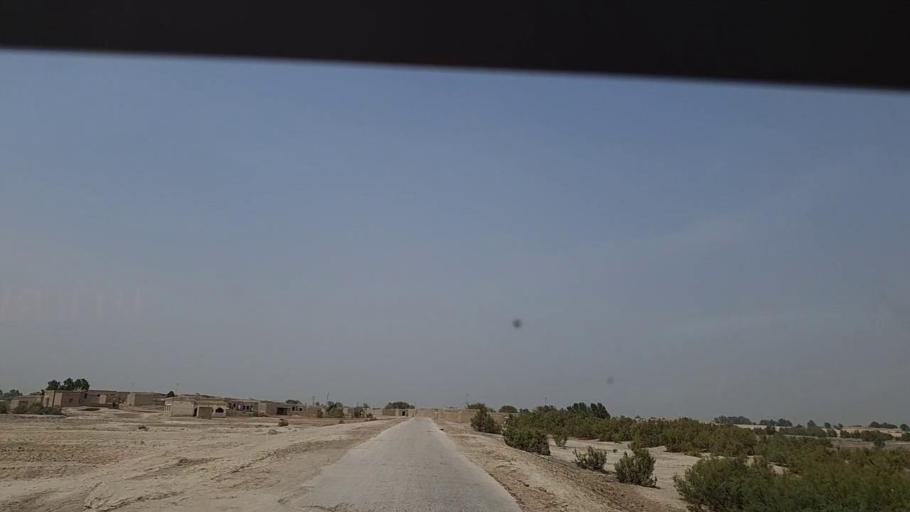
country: PK
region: Sindh
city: Khairpur Nathan Shah
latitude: 27.0658
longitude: 67.6493
